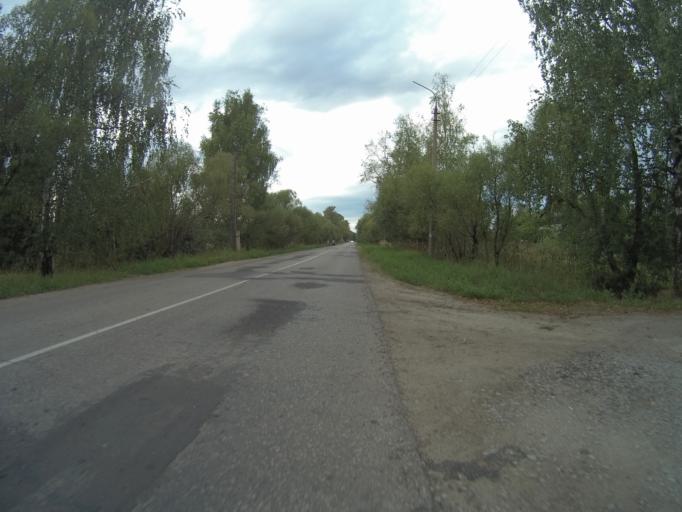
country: RU
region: Vladimir
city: Golovino
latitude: 55.9567
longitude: 40.4311
